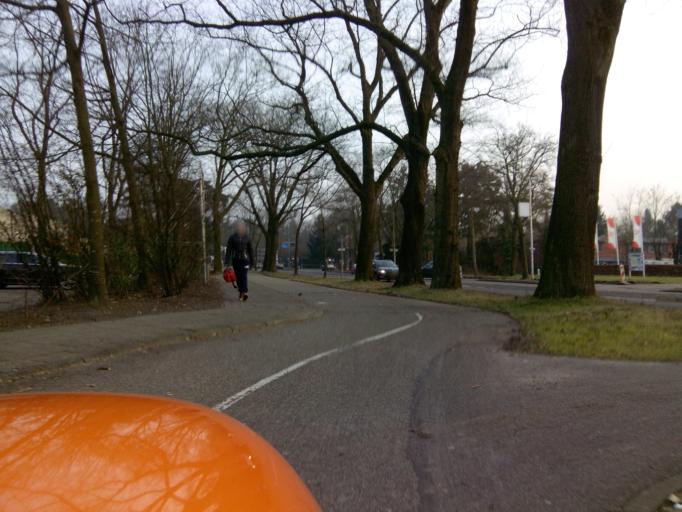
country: NL
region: Utrecht
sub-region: Gemeente Zeist
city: Zeist
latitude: 52.1027
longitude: 5.2543
